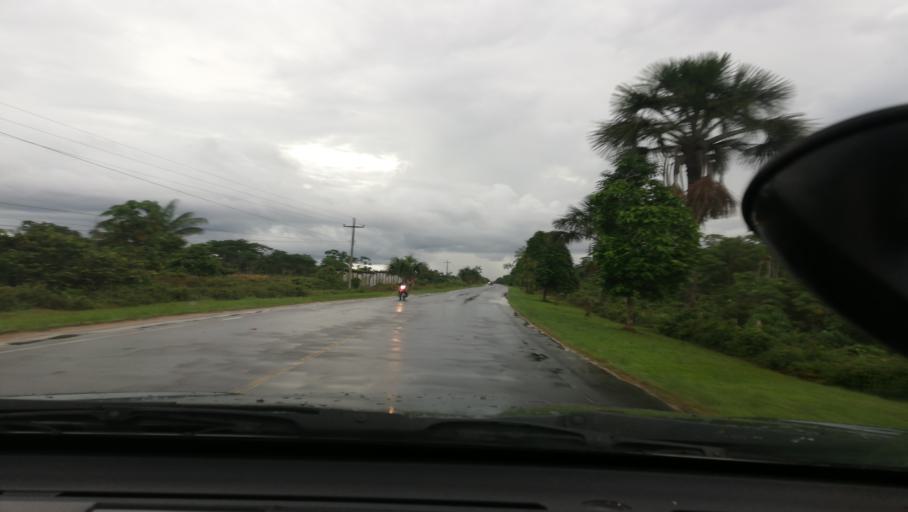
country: PE
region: Loreto
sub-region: Provincia de Maynas
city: Iquitos
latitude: -3.9016
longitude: -73.3527
